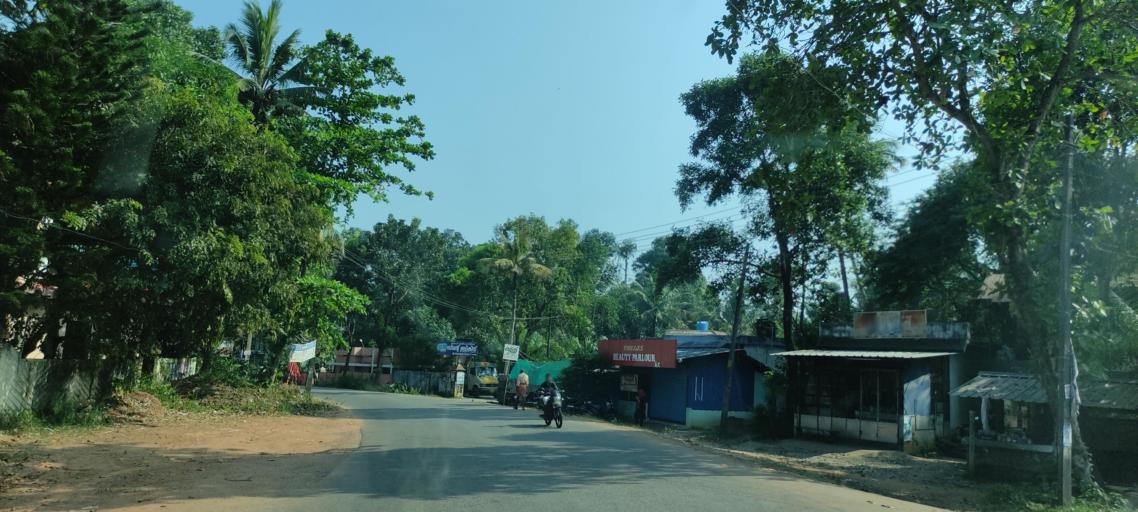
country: IN
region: Kerala
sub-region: Kollam
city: Panmana
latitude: 9.0491
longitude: 76.5669
